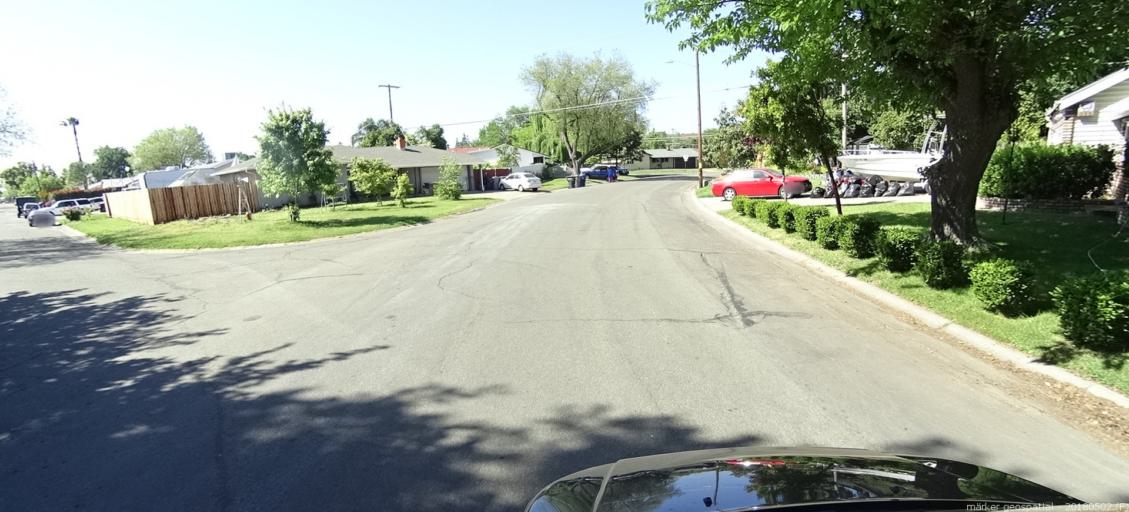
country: US
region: California
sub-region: Sacramento County
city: Arden-Arcade
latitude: 38.6046
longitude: -121.4231
